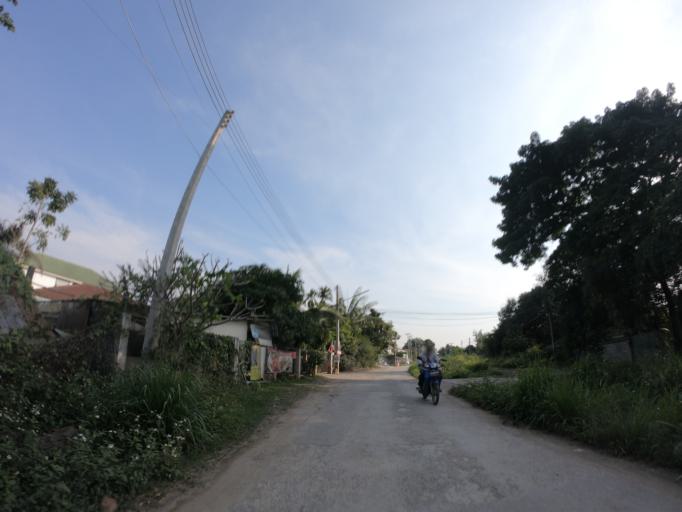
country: TH
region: Chiang Mai
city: Chiang Mai
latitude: 18.8271
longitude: 98.9929
